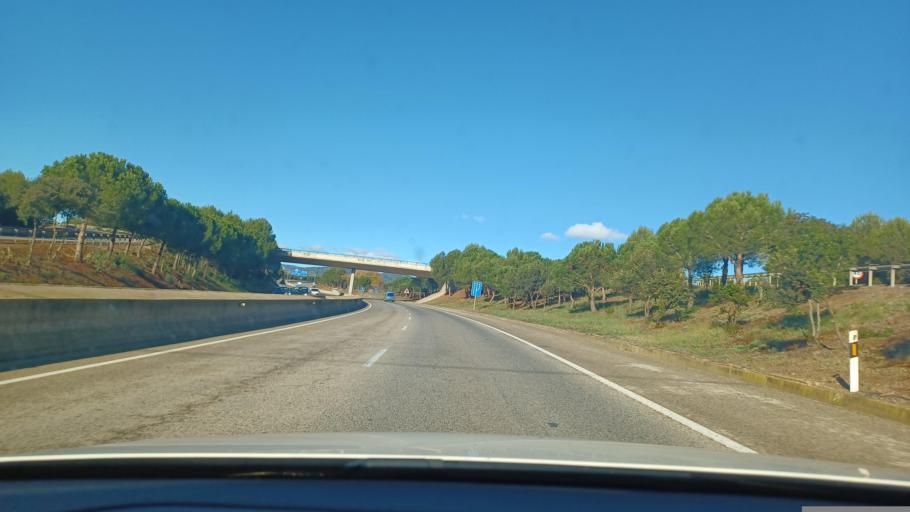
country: ES
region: Catalonia
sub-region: Provincia de Tarragona
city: Reus
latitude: 41.1674
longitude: 1.1402
